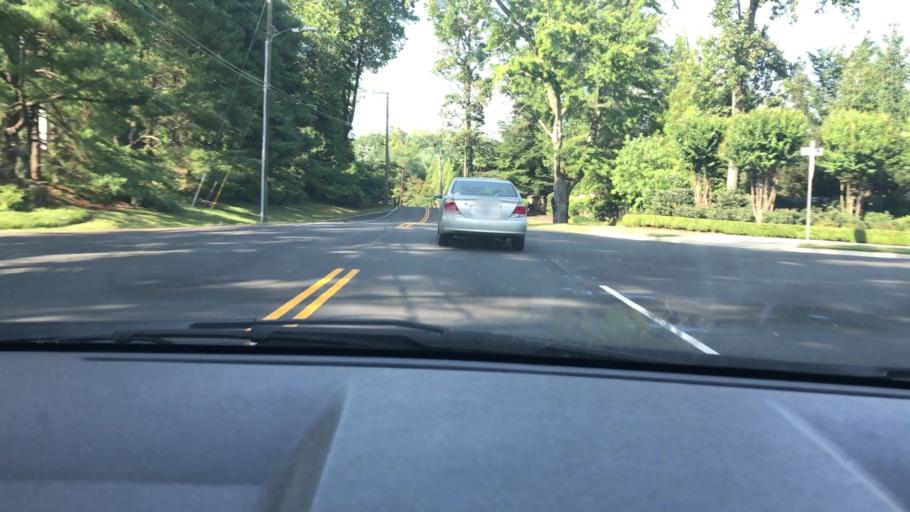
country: US
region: Virginia
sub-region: Fairfax County
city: Tysons Corner
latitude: 38.9483
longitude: -77.2269
